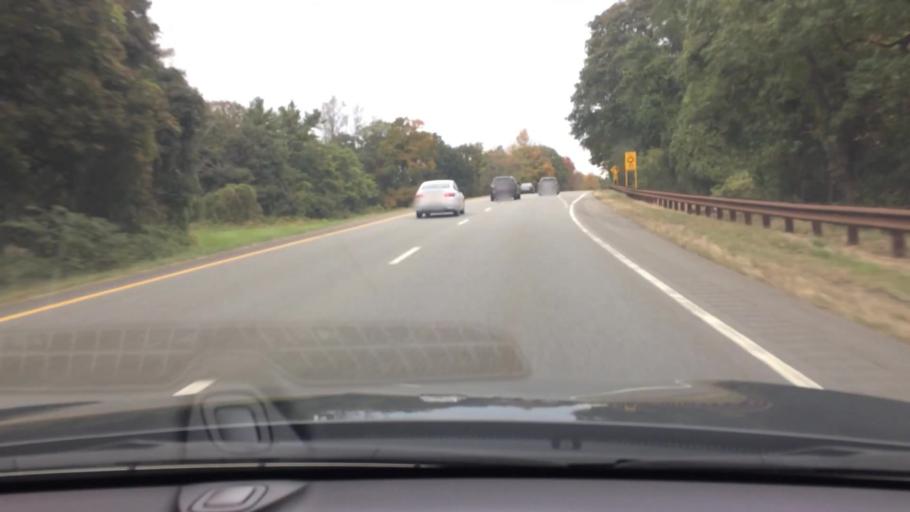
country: US
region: New Jersey
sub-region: Bergen County
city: Alpine
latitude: 40.9537
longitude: -73.9211
